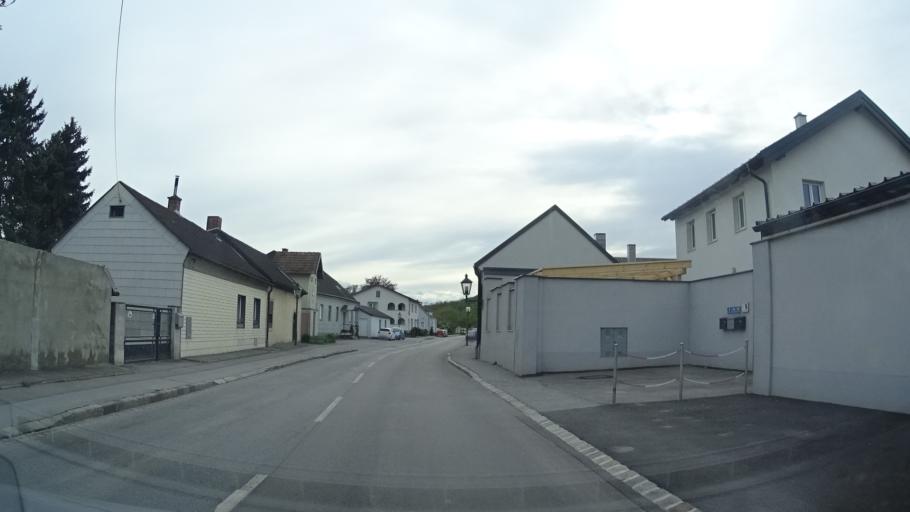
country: AT
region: Lower Austria
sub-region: Politischer Bezirk Korneuburg
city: Leobendorf
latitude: 48.3769
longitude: 16.3210
